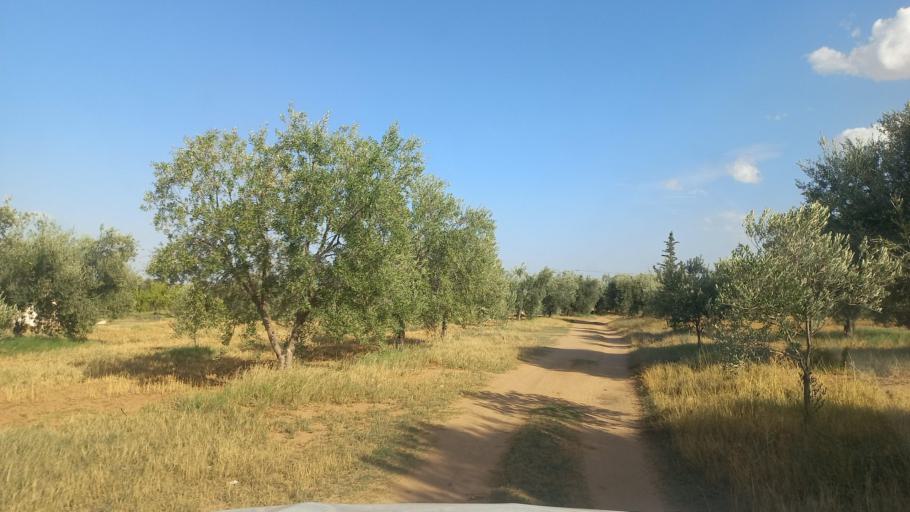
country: TN
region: Al Qasrayn
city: Kasserine
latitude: 35.2571
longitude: 9.0320
